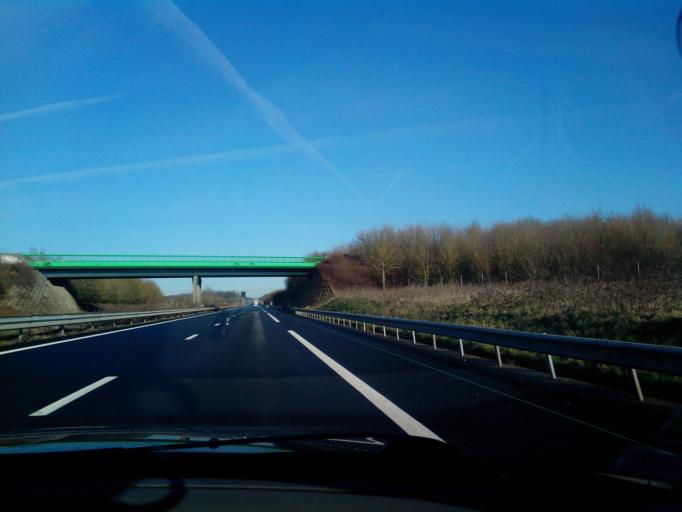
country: FR
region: Picardie
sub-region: Departement de l'Oise
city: Saint-Crepin-Ibouvillers
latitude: 49.3024
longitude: 2.0748
